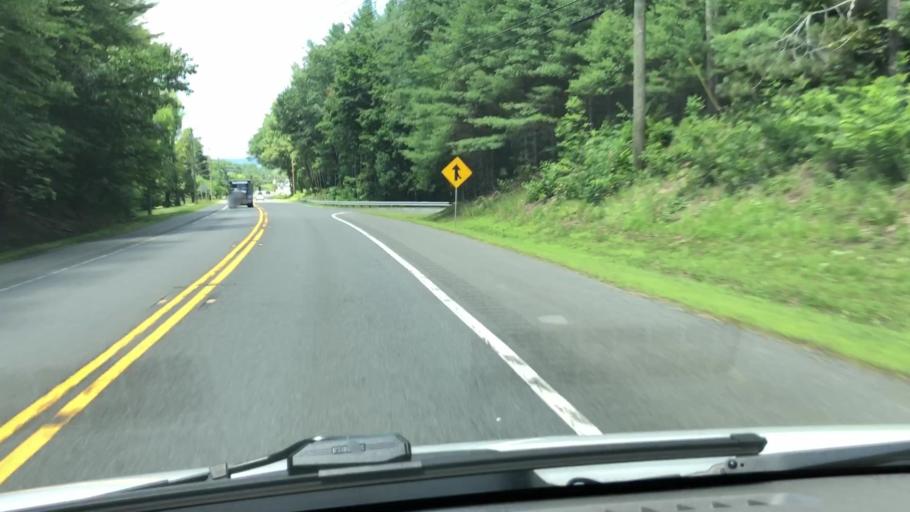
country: US
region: Massachusetts
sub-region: Hampshire County
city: North Amherst
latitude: 42.4477
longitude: -72.5562
